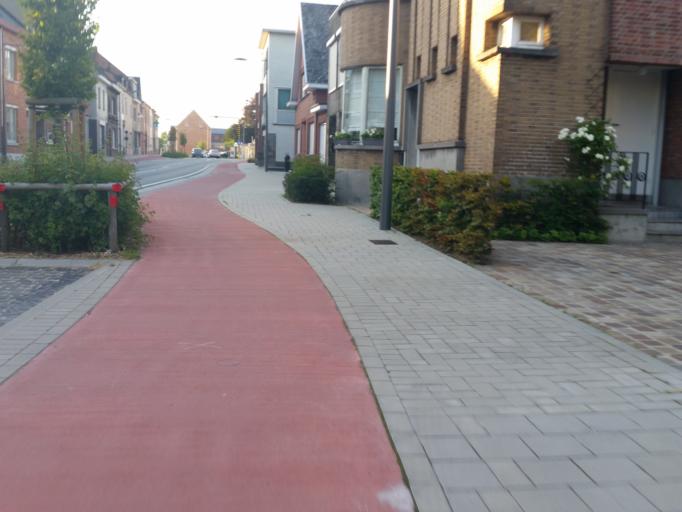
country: BE
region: Flanders
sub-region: Provincie Vlaams-Brabant
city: Steenokkerzeel
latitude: 50.9590
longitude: 4.4978
